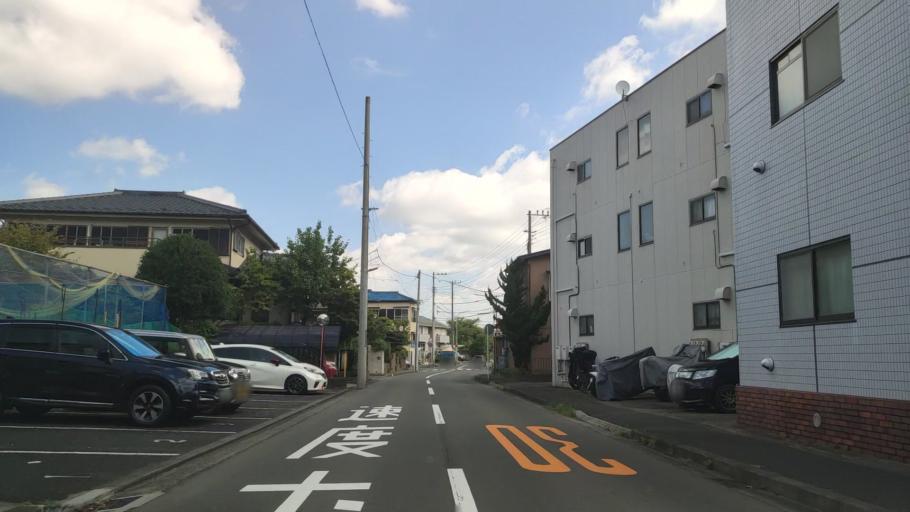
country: JP
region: Kanagawa
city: Yokohama
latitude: 35.5333
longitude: 139.6203
